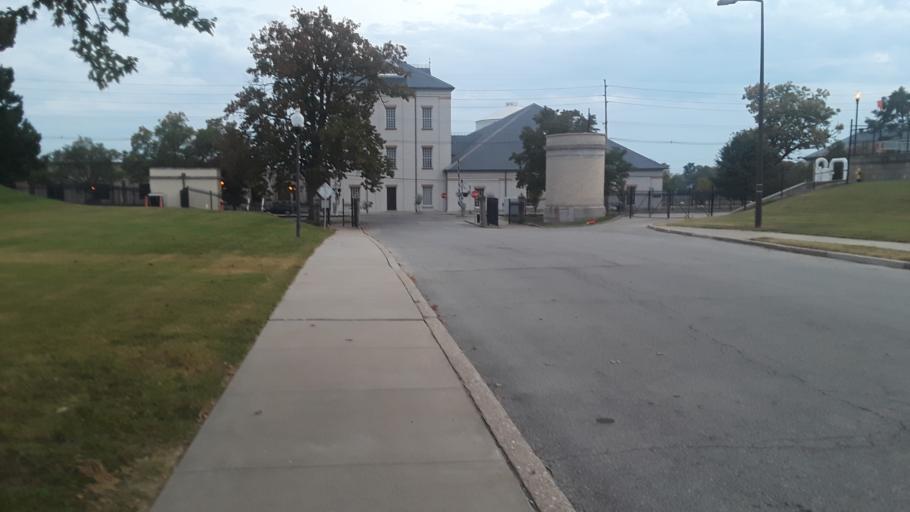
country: US
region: Kentucky
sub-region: Jefferson County
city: Indian Hills
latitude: 38.2554
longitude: -85.6807
